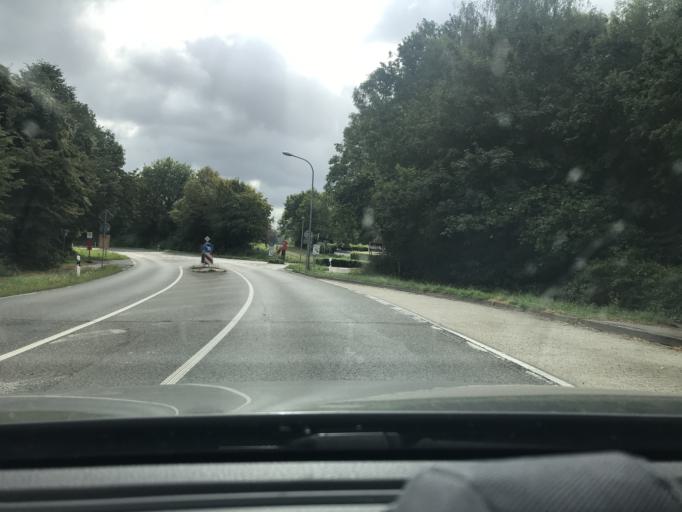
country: DE
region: North Rhine-Westphalia
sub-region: Regierungsbezirk Dusseldorf
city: Mettmann
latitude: 51.2287
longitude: 7.0030
